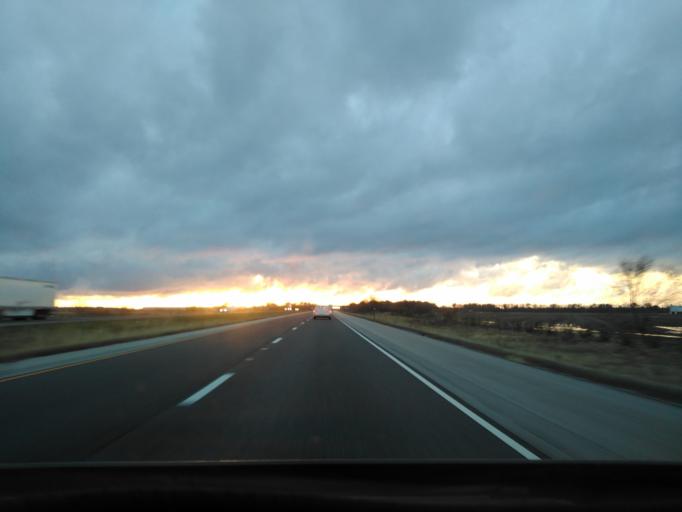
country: US
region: Illinois
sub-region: Fayette County
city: Saint Elmo
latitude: 39.0232
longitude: -88.8167
